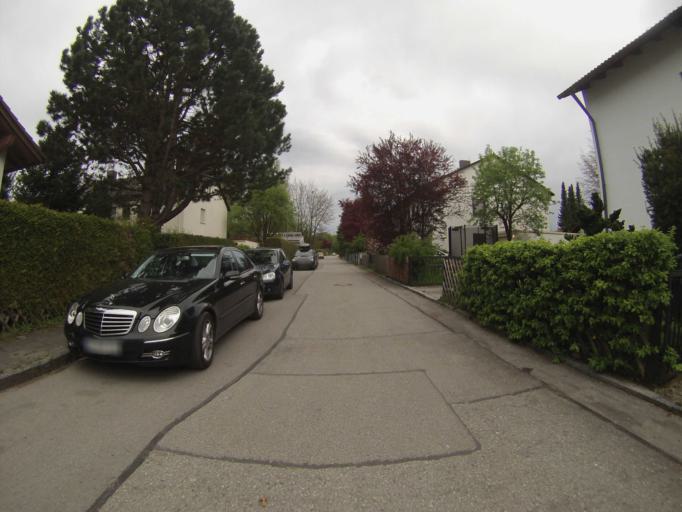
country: DE
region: Bavaria
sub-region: Upper Bavaria
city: Sauerlach
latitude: 47.9774
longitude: 11.6492
